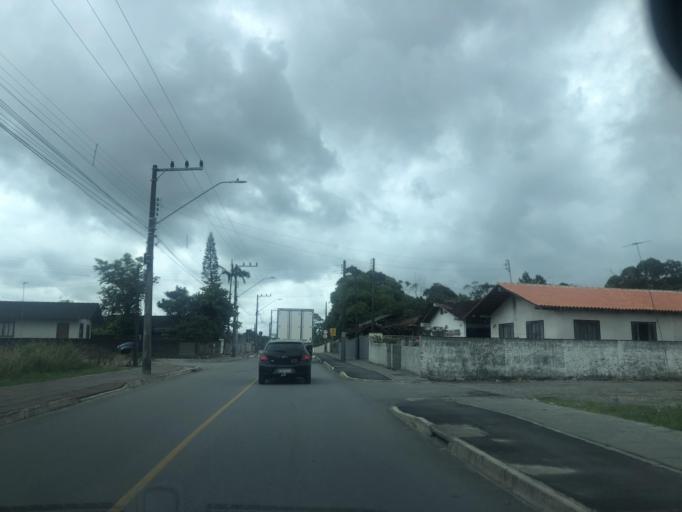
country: BR
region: Santa Catarina
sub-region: Joinville
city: Joinville
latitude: -26.3708
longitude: -48.7140
